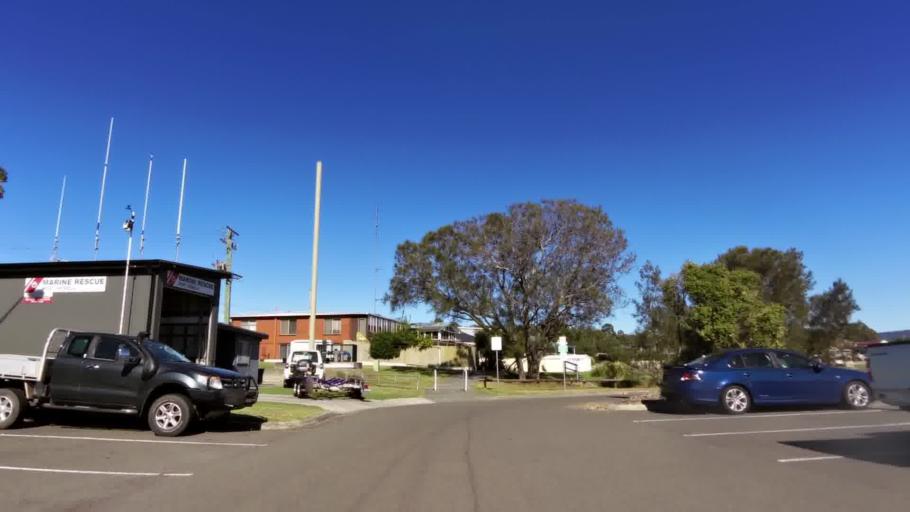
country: AU
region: New South Wales
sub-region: Shellharbour
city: Barrack Heights
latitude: -34.5553
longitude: 150.8339
